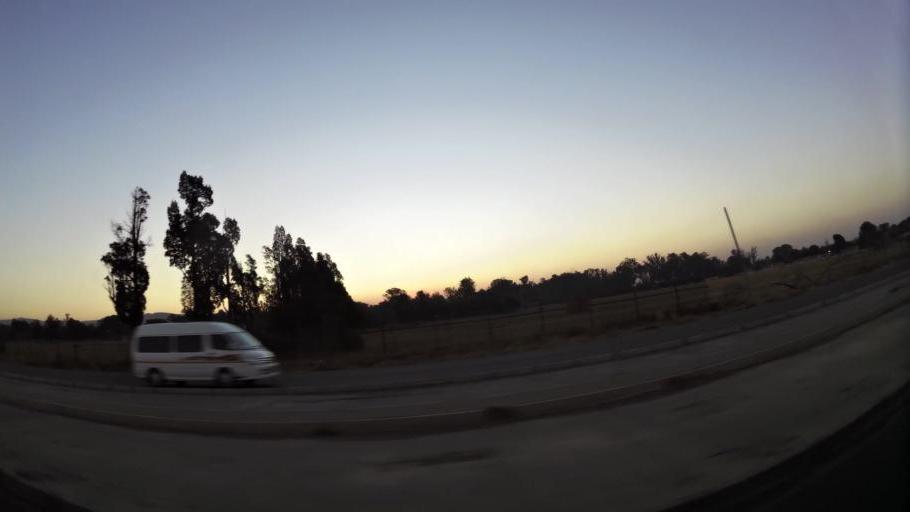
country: ZA
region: North-West
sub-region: Bojanala Platinum District Municipality
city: Rustenburg
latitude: -25.6414
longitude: 27.2627
